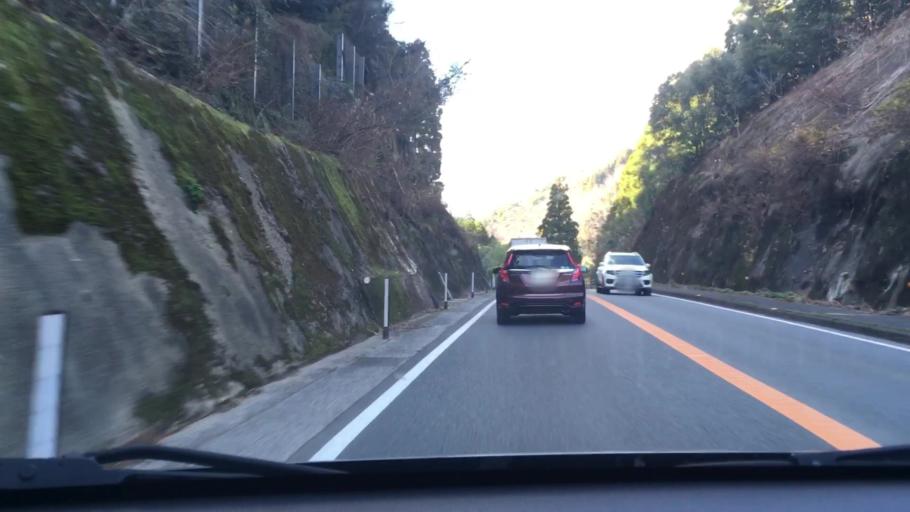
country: JP
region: Oita
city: Tsukumiura
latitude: 33.0002
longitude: 131.8127
